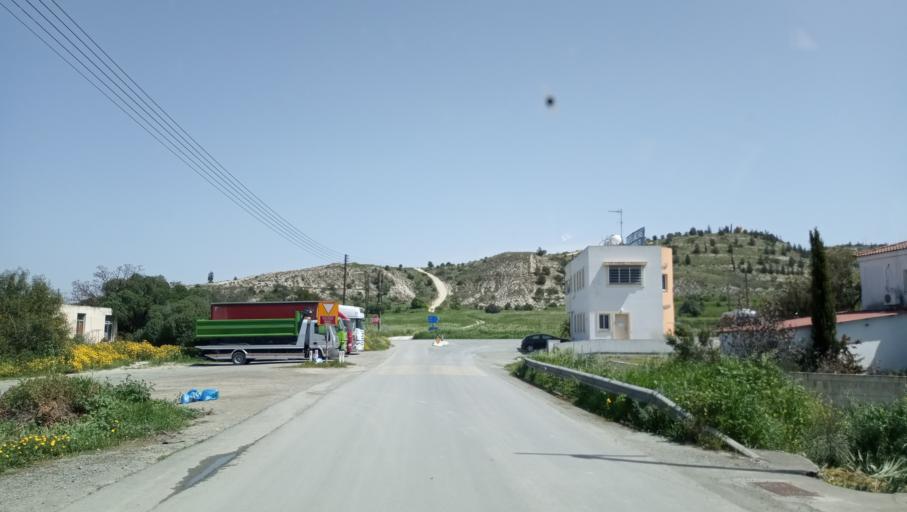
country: CY
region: Lefkosia
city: Alampra
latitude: 35.0071
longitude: 33.3931
